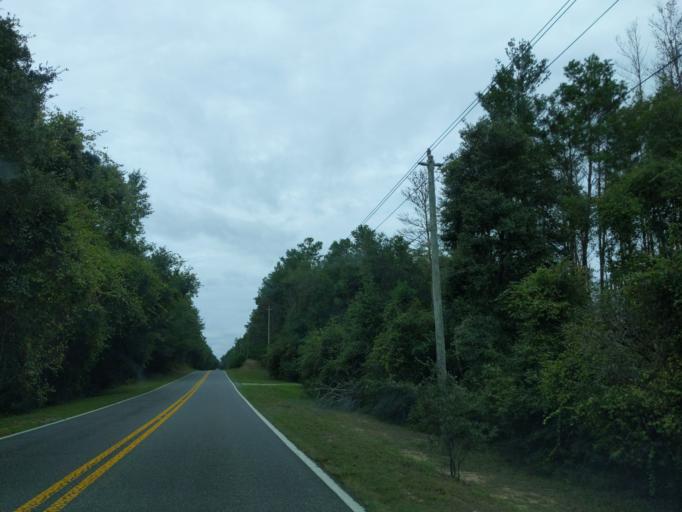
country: US
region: Florida
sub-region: Leon County
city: Woodville
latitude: 30.3683
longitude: -84.1736
